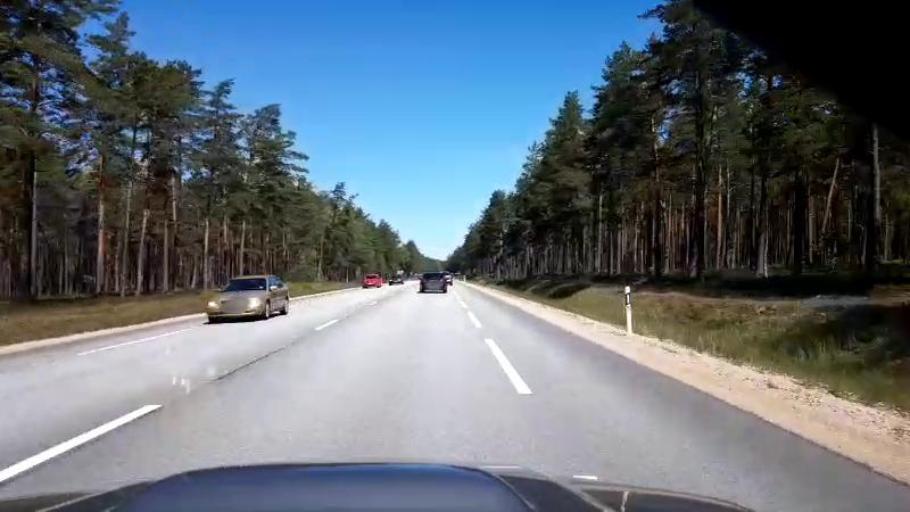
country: LV
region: Carnikava
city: Carnikava
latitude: 57.1719
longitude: 24.3434
